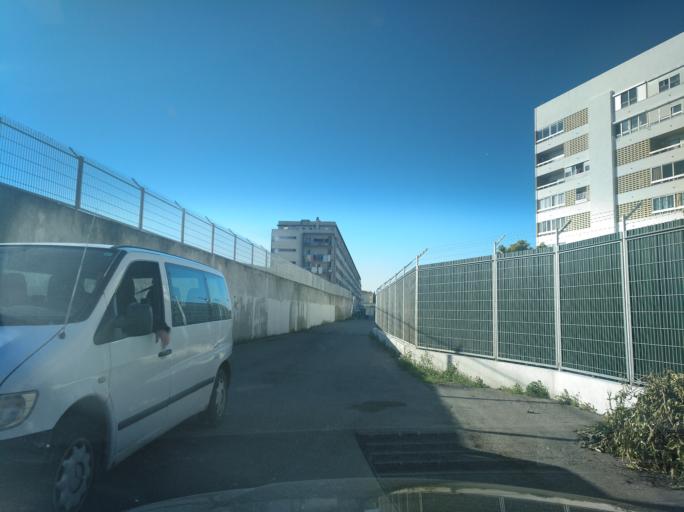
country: PT
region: Lisbon
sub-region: Loures
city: Moscavide
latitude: 38.7807
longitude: -9.1149
